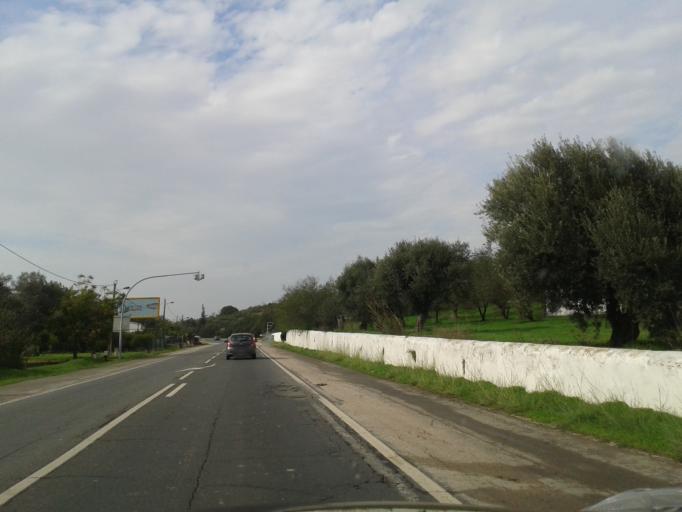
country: PT
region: Faro
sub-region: Loule
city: Boliqueime
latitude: 37.1232
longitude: -8.1910
